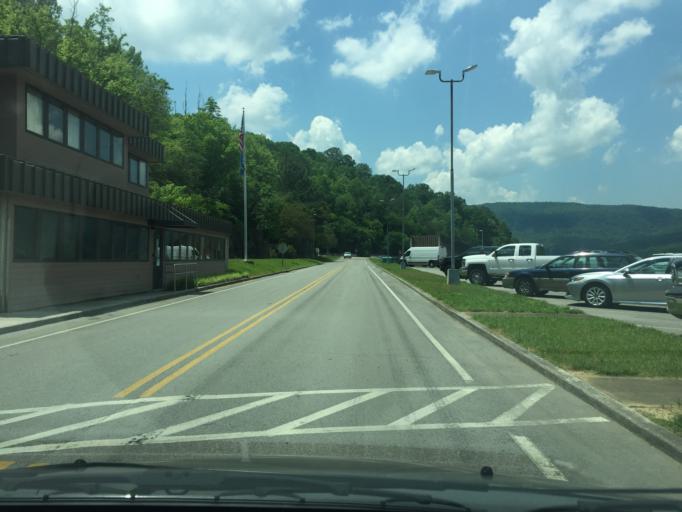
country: US
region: Tennessee
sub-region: Hamilton County
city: Signal Mountain
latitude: 35.0622
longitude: -85.4082
